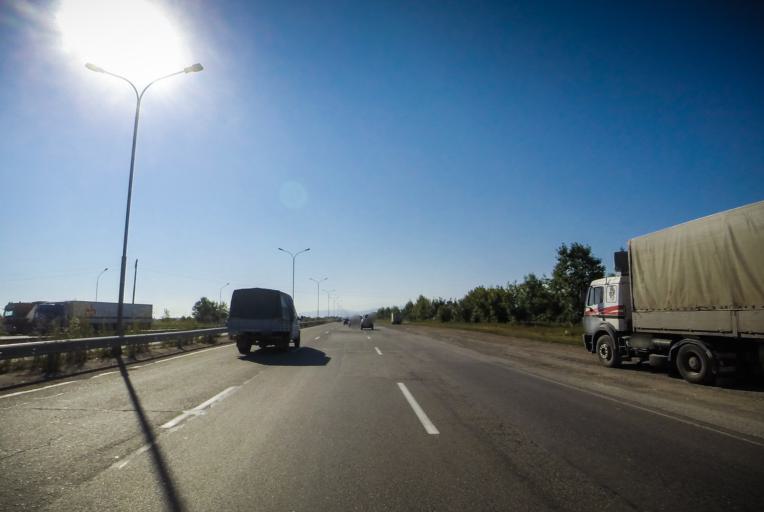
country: RU
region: North Ossetia
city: Nogir
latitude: 43.0778
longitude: 44.5995
